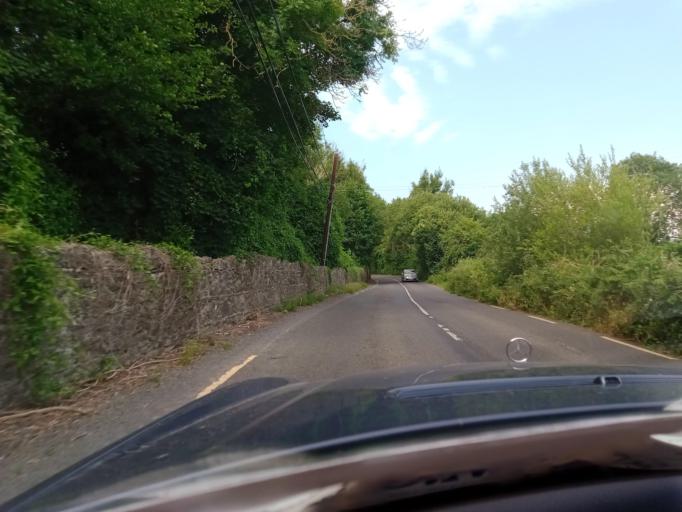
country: IE
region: Munster
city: Carrick-on-Suir
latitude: 52.3764
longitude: -7.3907
